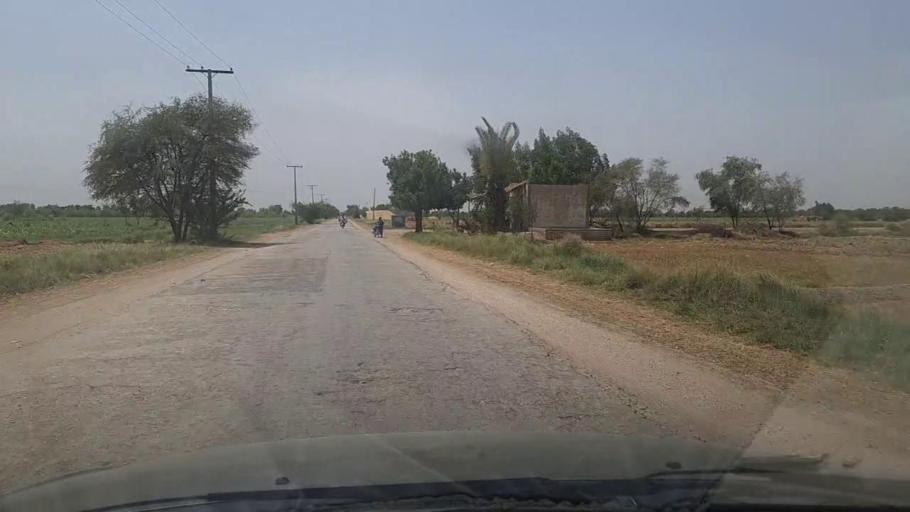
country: PK
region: Sindh
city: Bhiria
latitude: 26.8939
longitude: 68.2444
